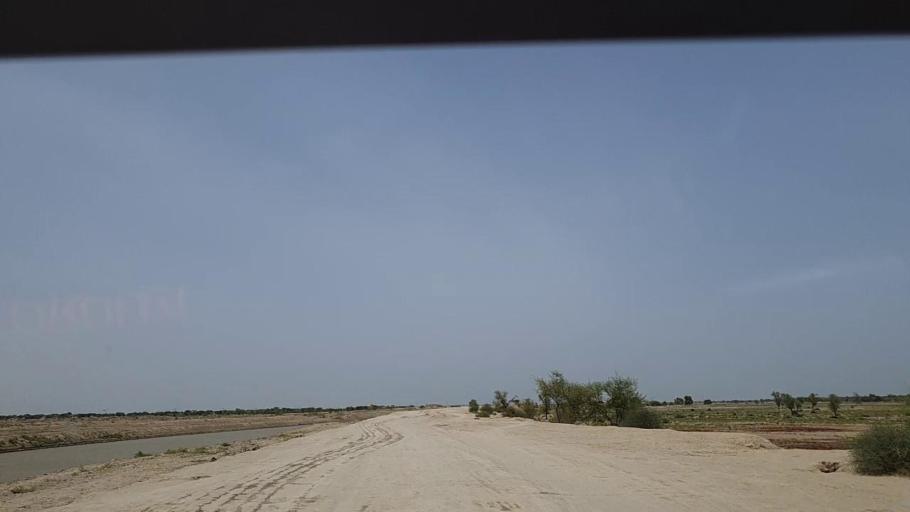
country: PK
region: Sindh
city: Johi
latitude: 26.7330
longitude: 67.6831
